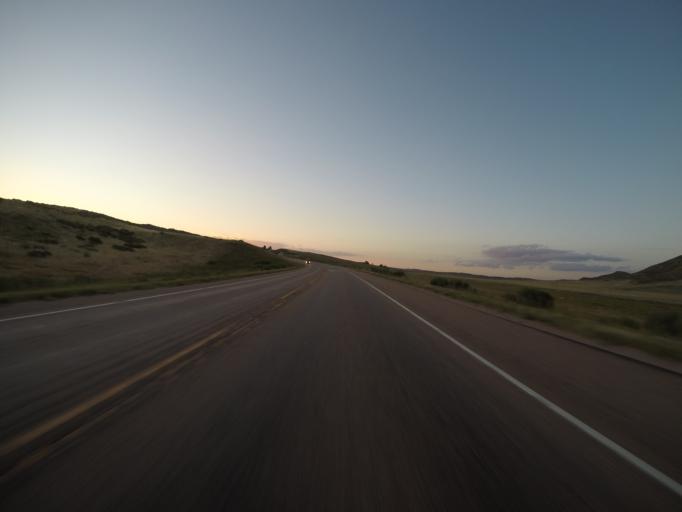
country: US
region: Colorado
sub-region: Larimer County
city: Laporte
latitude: 40.7555
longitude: -105.1710
